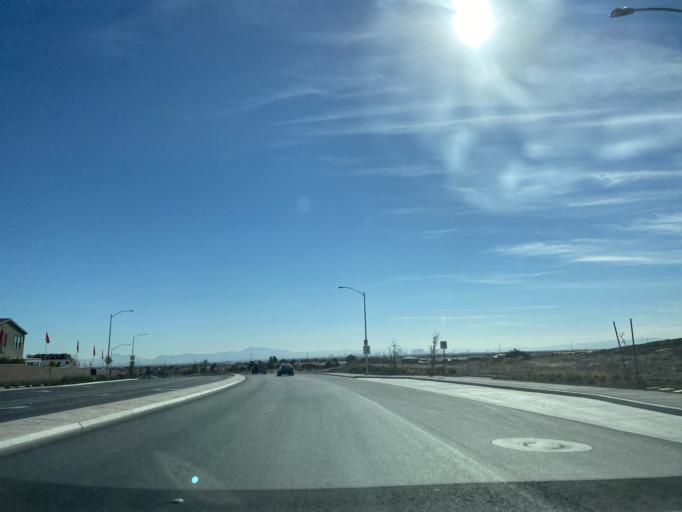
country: US
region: Nevada
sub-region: Clark County
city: North Las Vegas
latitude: 36.2873
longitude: -115.1532
